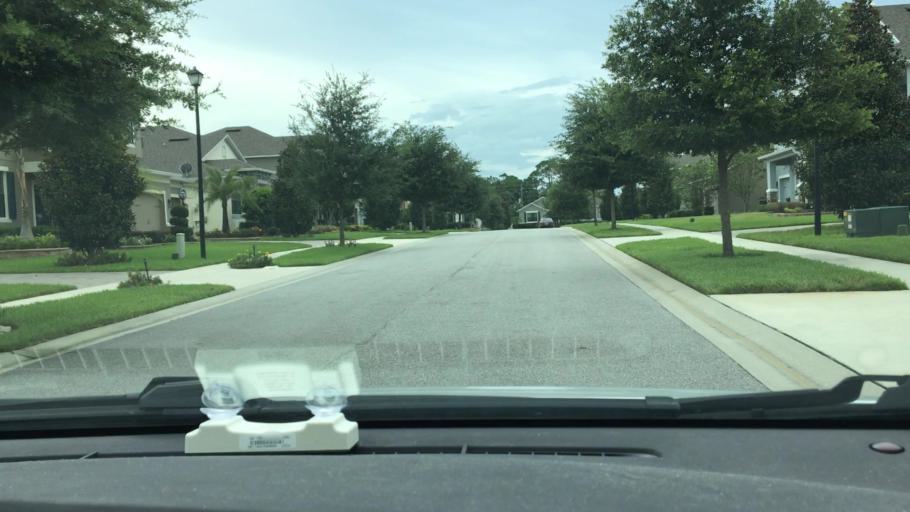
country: US
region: Florida
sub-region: Seminole County
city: Heathrow
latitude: 28.8177
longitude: -81.3609
